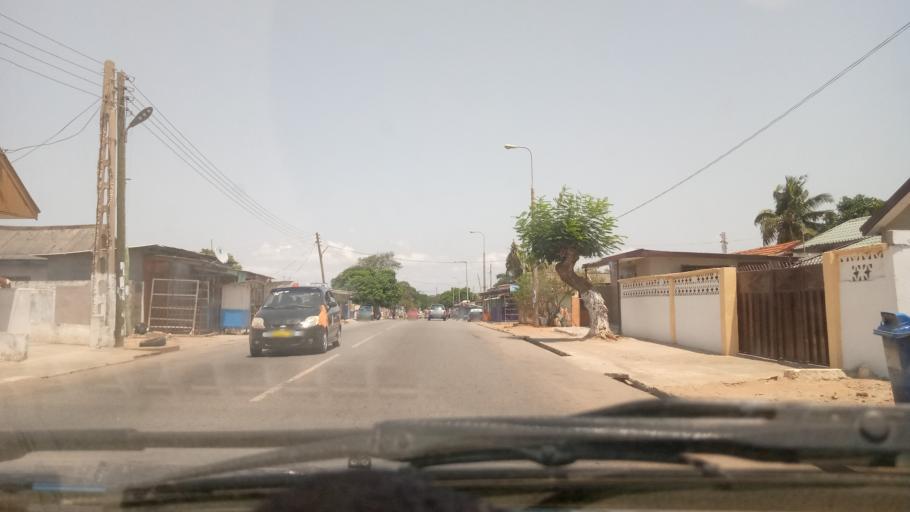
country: GH
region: Greater Accra
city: Accra
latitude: 5.5356
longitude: -0.2380
